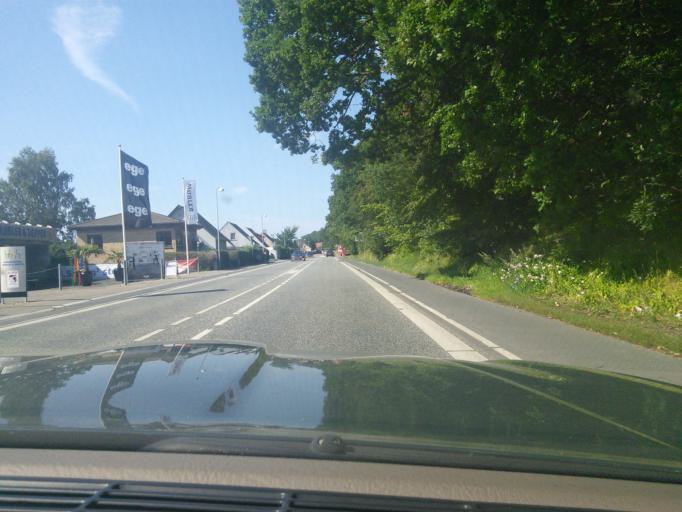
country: DK
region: Capital Region
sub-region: Halsnaes Kommune
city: Frederiksvaerk
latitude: 55.9829
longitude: 12.0201
